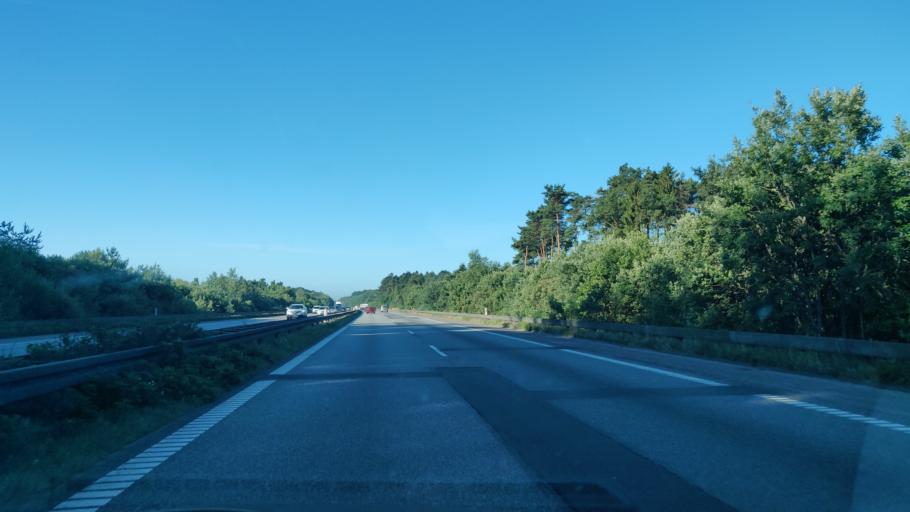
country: DK
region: North Denmark
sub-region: Alborg Kommune
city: Svenstrup
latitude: 56.9311
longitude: 9.8494
